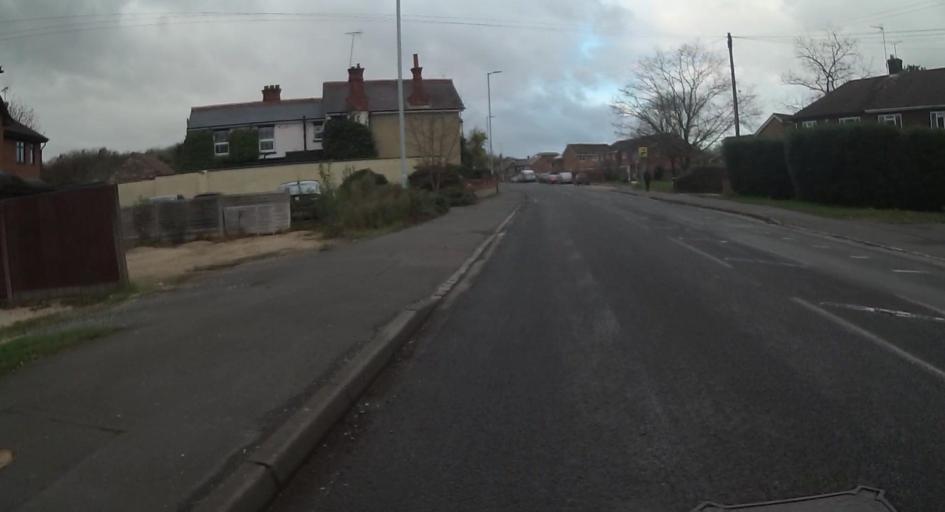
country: GB
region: England
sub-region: Bracknell Forest
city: Sandhurst
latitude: 51.3433
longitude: -0.7836
